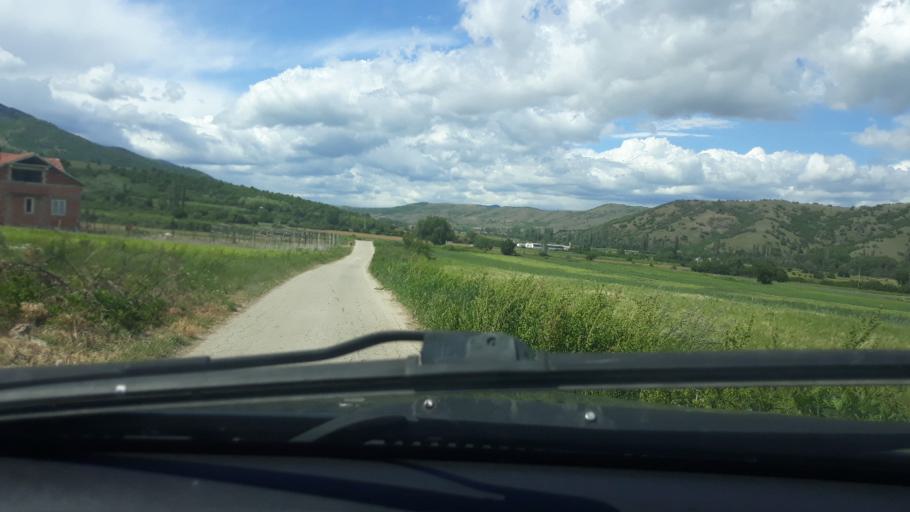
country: MK
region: Krivogastani
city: Krivogashtani
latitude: 41.3407
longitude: 21.2998
